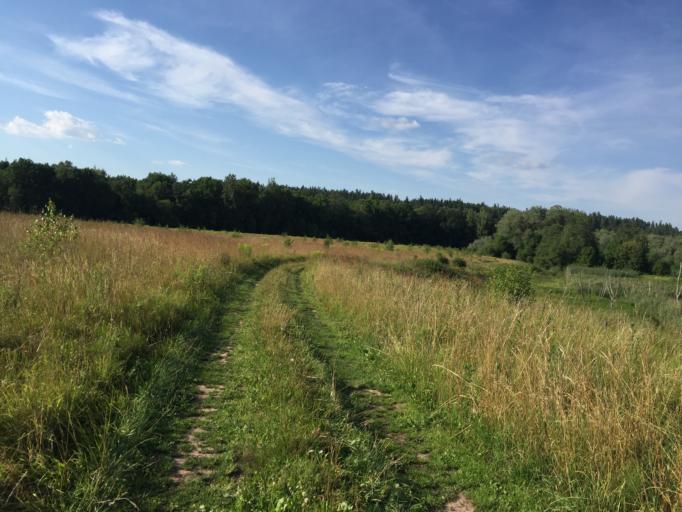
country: LV
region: Krimulda
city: Ragana
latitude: 57.1464
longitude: 24.7599
